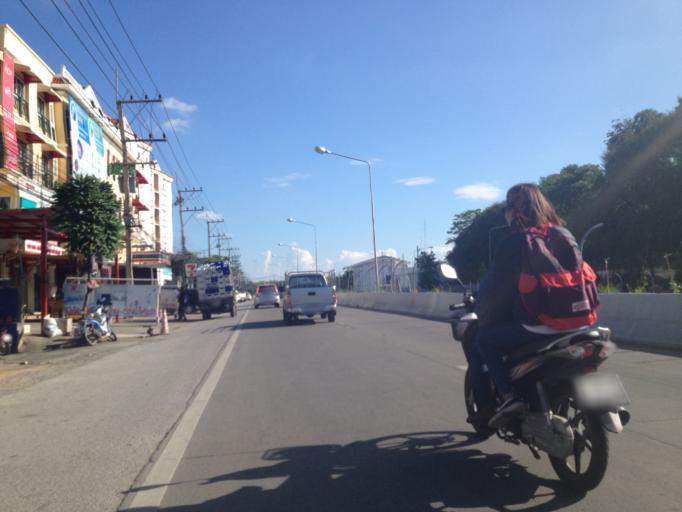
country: TH
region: Chiang Mai
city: Chiang Mai
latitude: 18.7997
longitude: 98.9608
